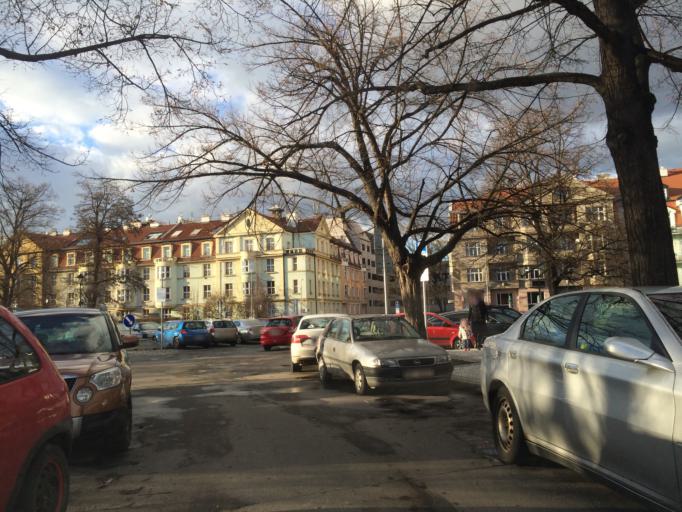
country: CZ
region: Praha
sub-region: Praha 1
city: Mala Strana
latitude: 50.0957
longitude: 14.4061
